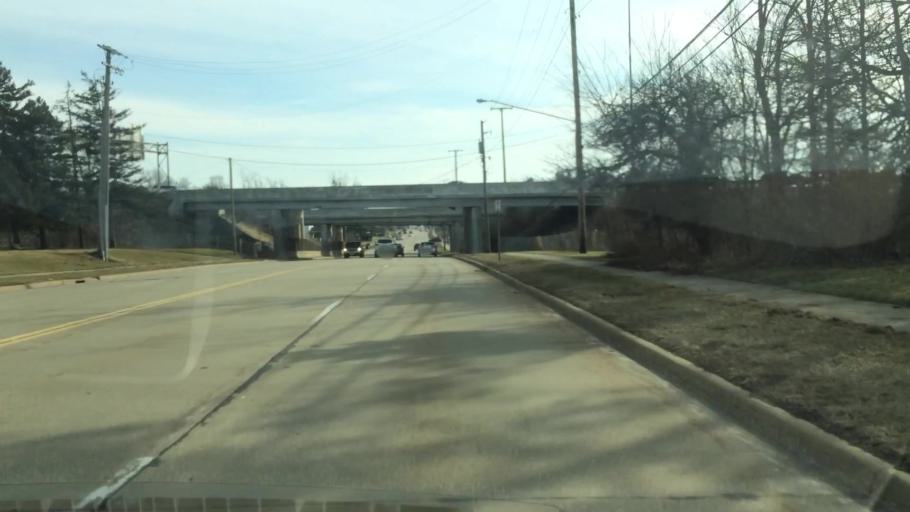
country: US
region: Ohio
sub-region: Cuyahoga County
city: Orange
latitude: 41.4307
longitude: -81.4980
